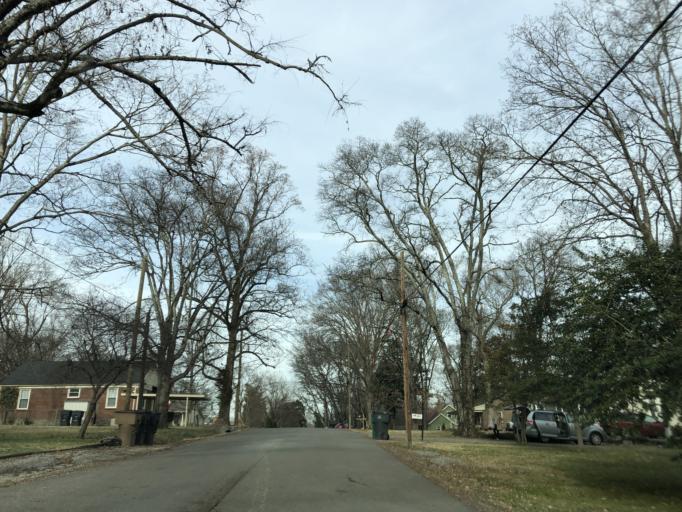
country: US
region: Tennessee
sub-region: Davidson County
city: Nashville
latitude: 36.2147
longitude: -86.7276
